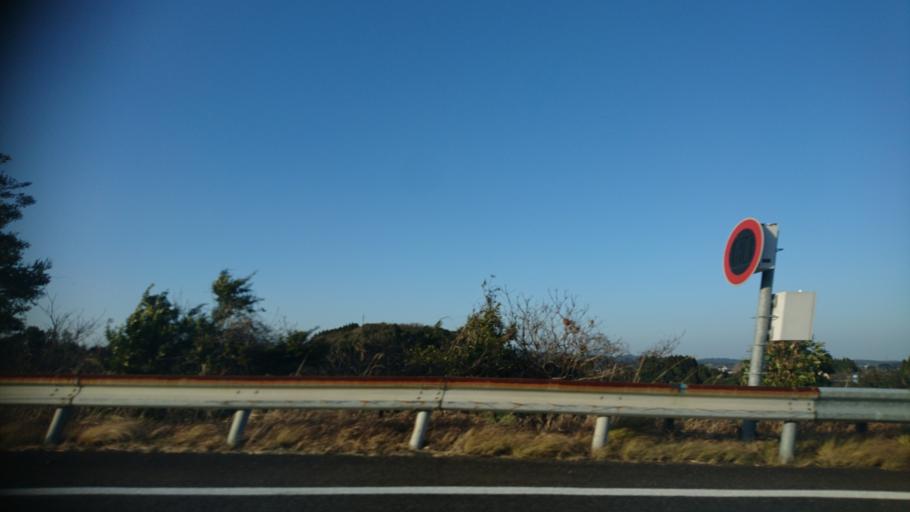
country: JP
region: Miyazaki
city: Miyazaki-shi
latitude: 31.8206
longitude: 131.2858
